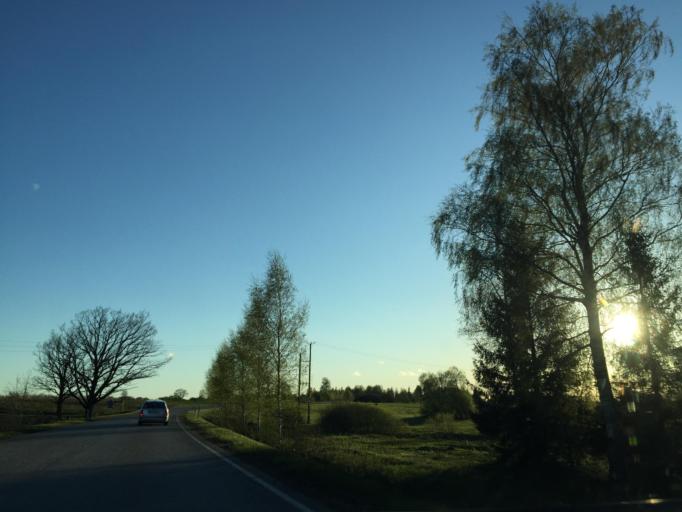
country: LV
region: Skriveri
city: Skriveri
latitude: 56.8830
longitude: 25.2632
